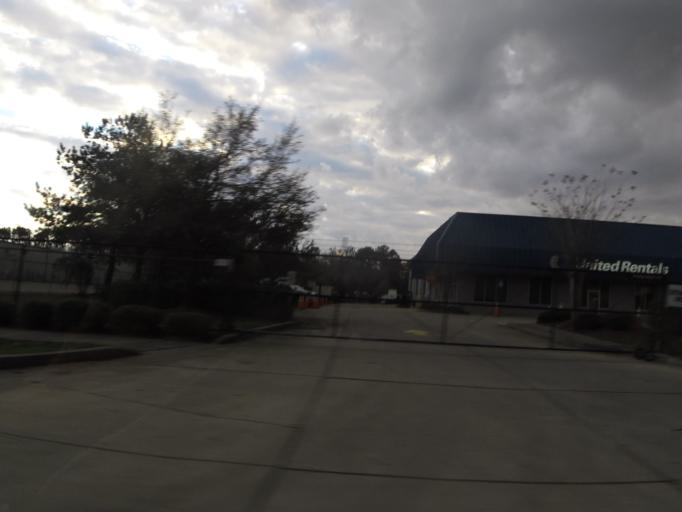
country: US
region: Florida
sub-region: Saint Johns County
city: Fruit Cove
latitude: 30.1933
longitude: -81.5721
